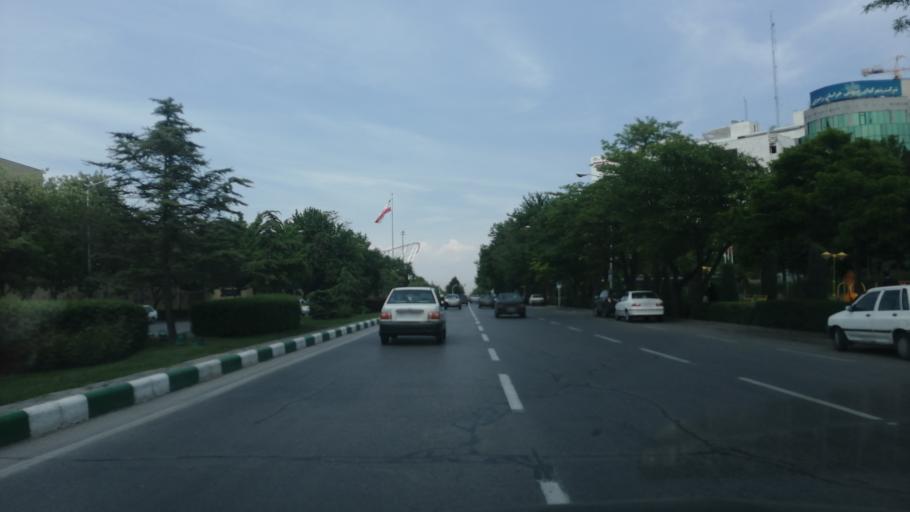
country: IR
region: Razavi Khorasan
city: Mashhad
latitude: 36.3222
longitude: 59.5680
